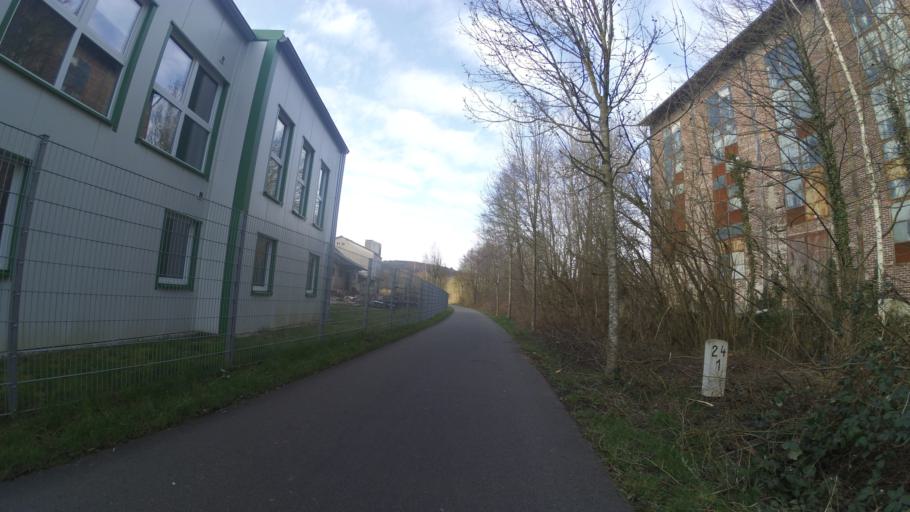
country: DE
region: Saarland
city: Gersheim
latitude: 49.1513
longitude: 7.2087
